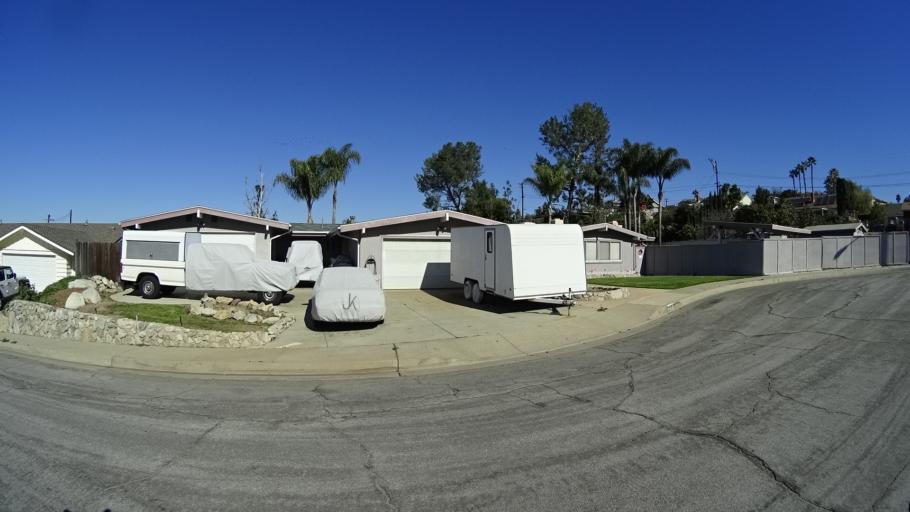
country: US
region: California
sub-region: Orange County
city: Villa Park
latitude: 33.8412
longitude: -117.8380
